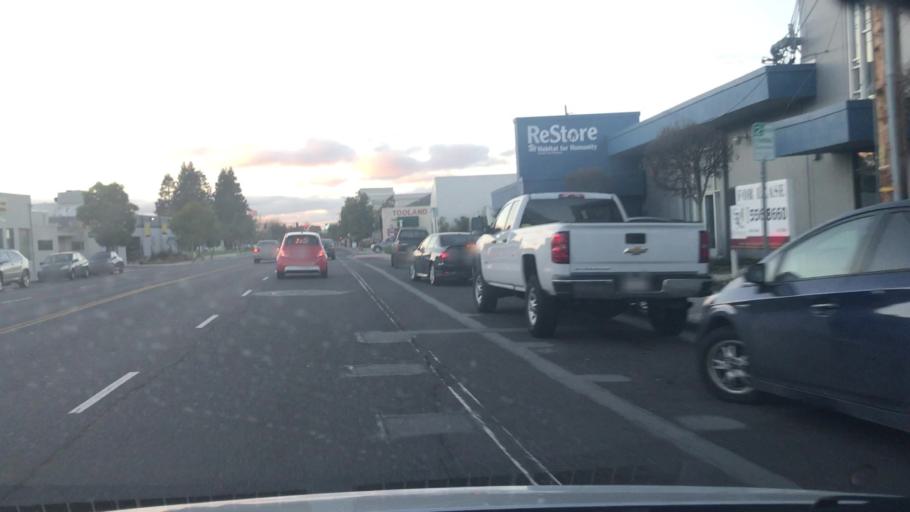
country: US
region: California
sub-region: San Mateo County
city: Redwood City
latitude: 37.5003
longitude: -122.2440
